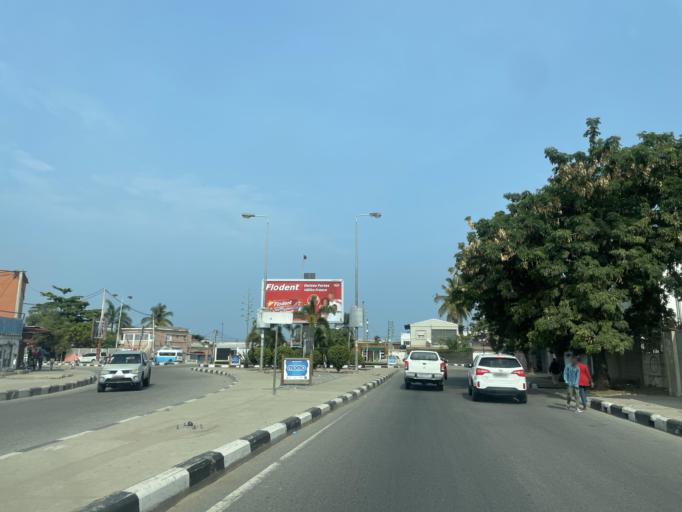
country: AO
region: Luanda
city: Luanda
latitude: -8.8297
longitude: 13.2175
